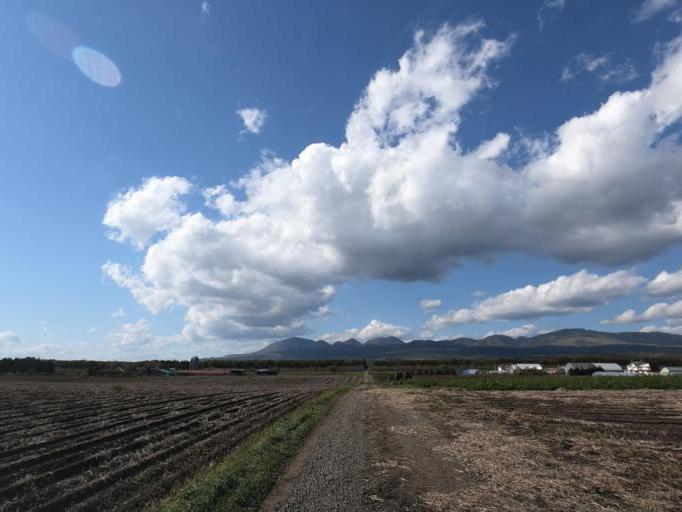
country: JP
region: Hokkaido
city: Otofuke
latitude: 43.2356
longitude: 143.2595
